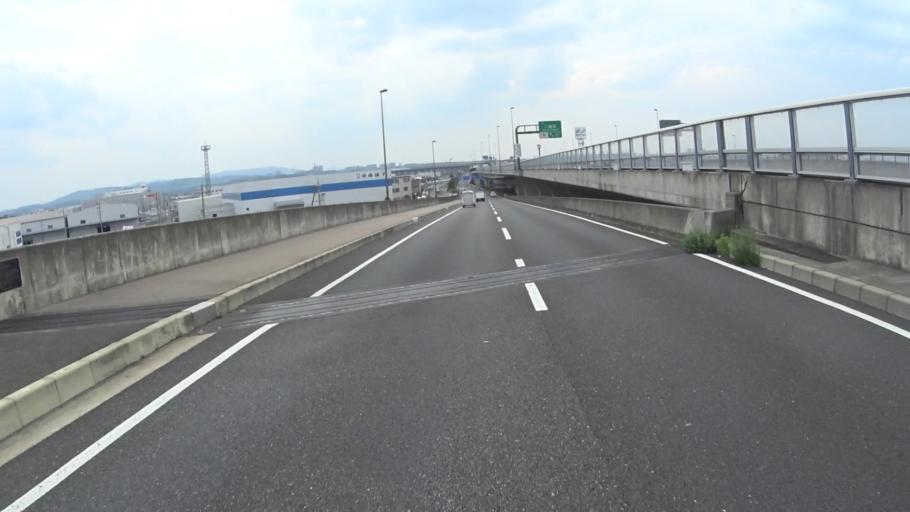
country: JP
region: Kyoto
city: Yawata
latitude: 34.8692
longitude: 135.7415
